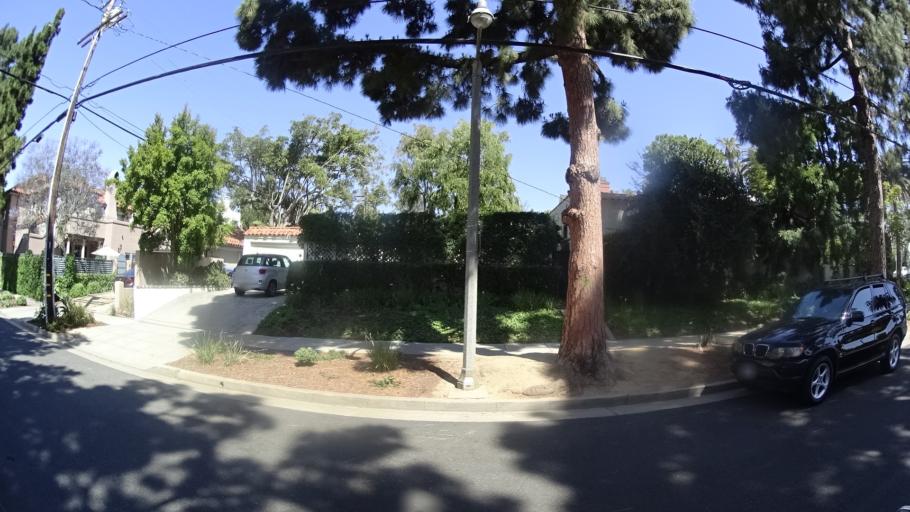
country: US
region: California
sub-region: Los Angeles County
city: Santa Monica
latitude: 34.0381
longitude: -118.4908
